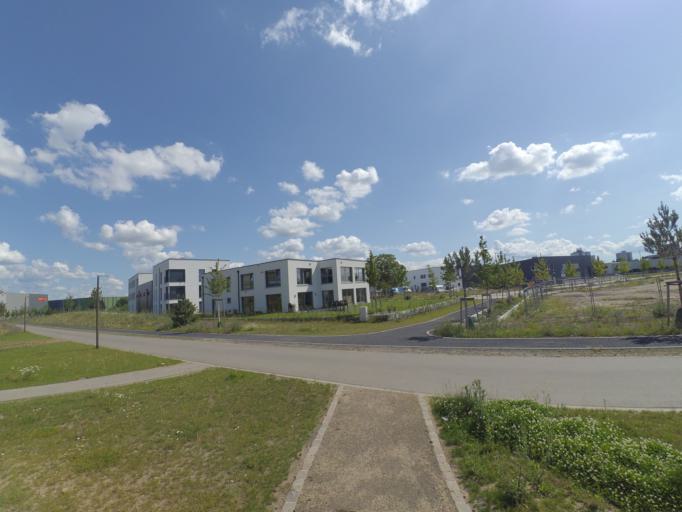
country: DE
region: Hesse
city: Viernheim
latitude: 49.5171
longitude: 8.5506
